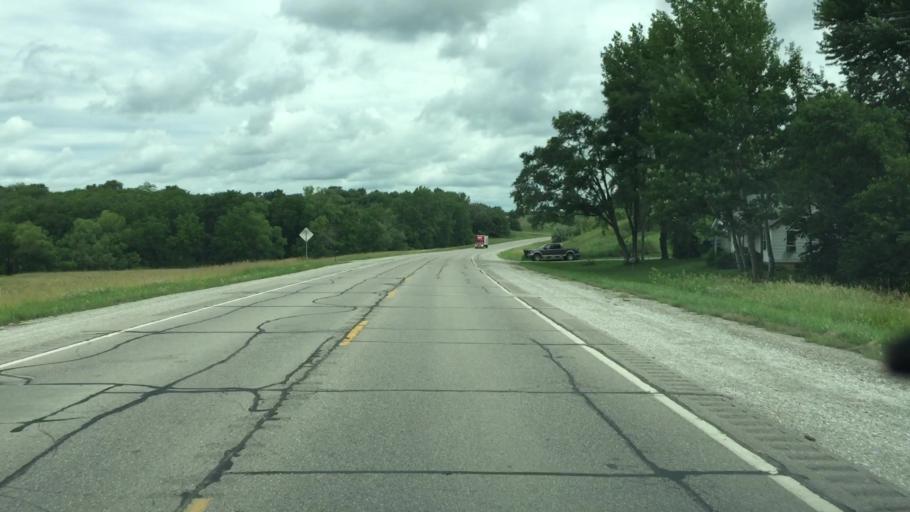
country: US
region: Iowa
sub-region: Jasper County
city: Monroe
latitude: 41.5315
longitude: -93.1019
